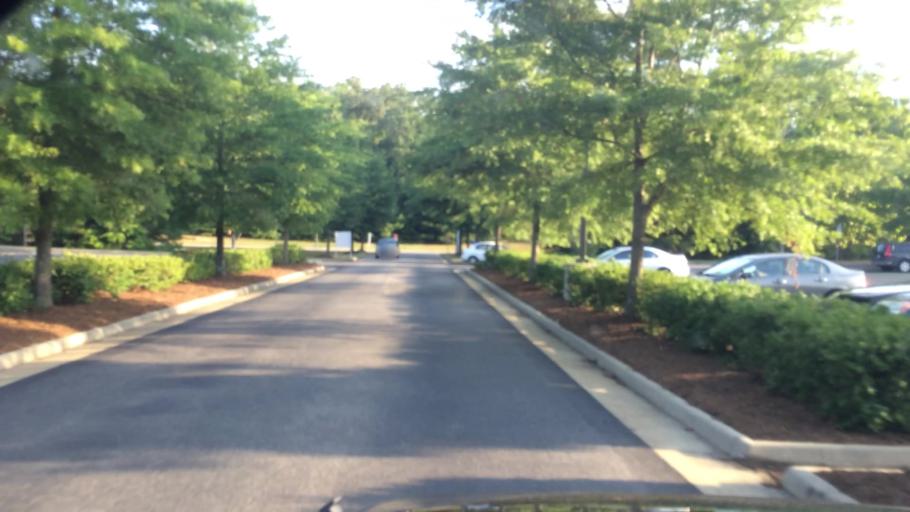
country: US
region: Virginia
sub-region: James City County
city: Williamsburg
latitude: 37.3380
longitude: -76.7419
